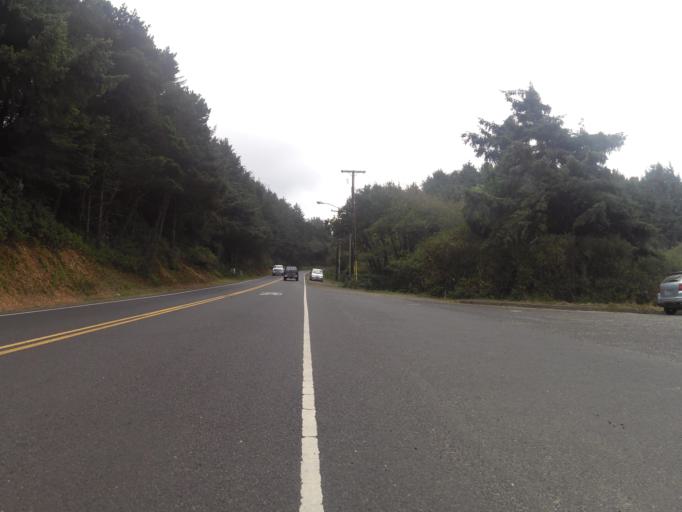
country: US
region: Oregon
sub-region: Lincoln County
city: Newport
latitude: 44.6584
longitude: -124.0556
